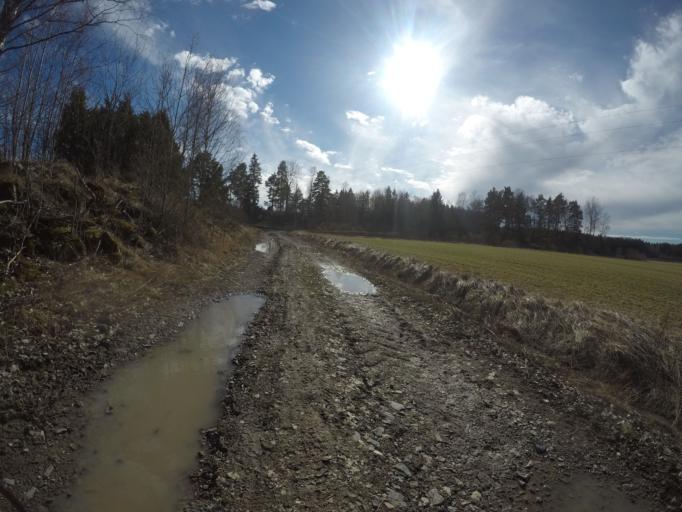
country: SE
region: Soedermanland
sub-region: Eskilstuna Kommun
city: Kvicksund
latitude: 59.4283
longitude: 16.2892
